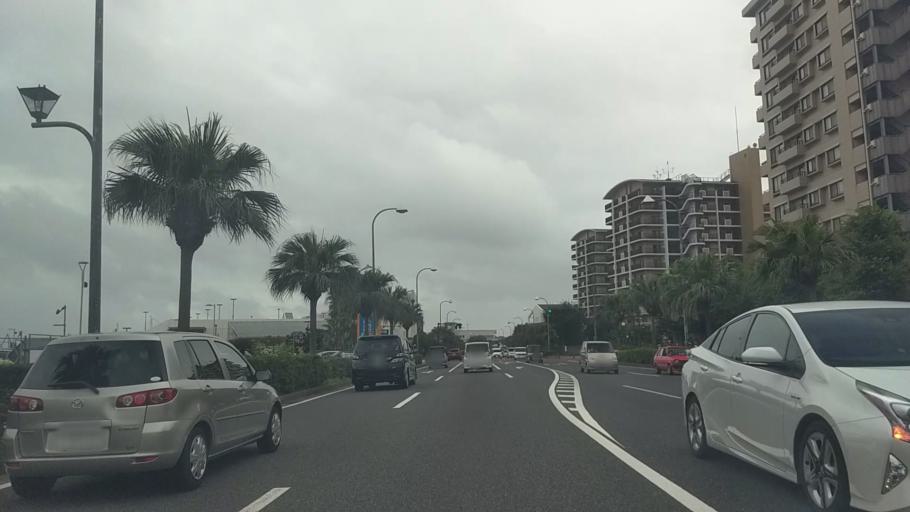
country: JP
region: Kanagawa
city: Yokosuka
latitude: 35.2736
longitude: 139.6836
